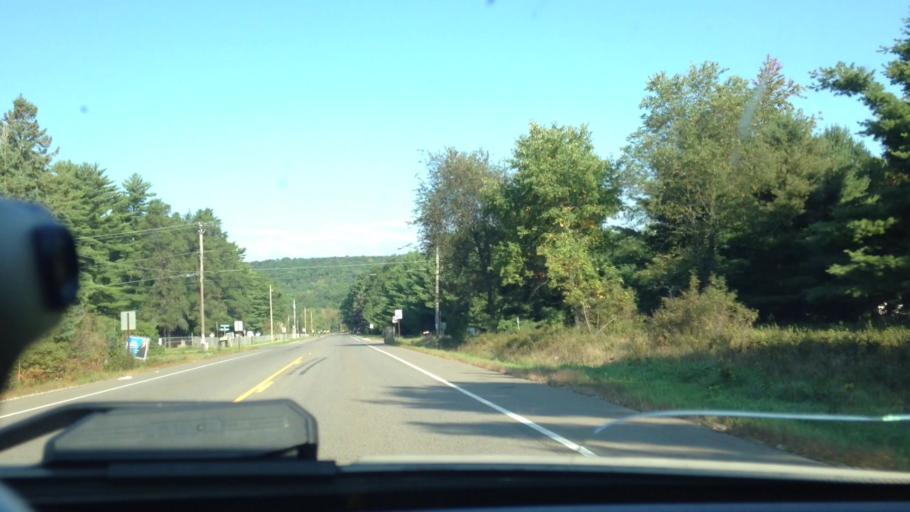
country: US
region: Michigan
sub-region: Dickinson County
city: Quinnesec
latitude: 45.8387
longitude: -88.0121
